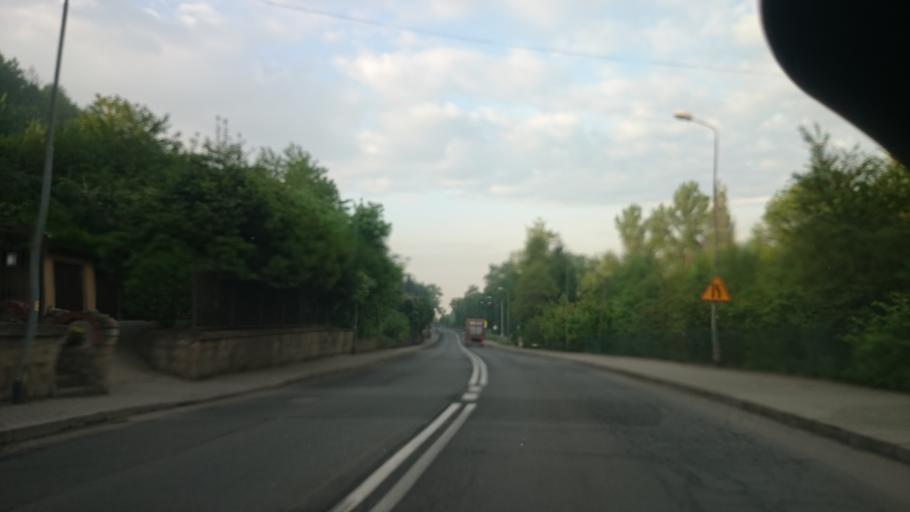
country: PL
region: Lower Silesian Voivodeship
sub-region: Powiat klodzki
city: Klodzko
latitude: 50.4487
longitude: 16.6601
